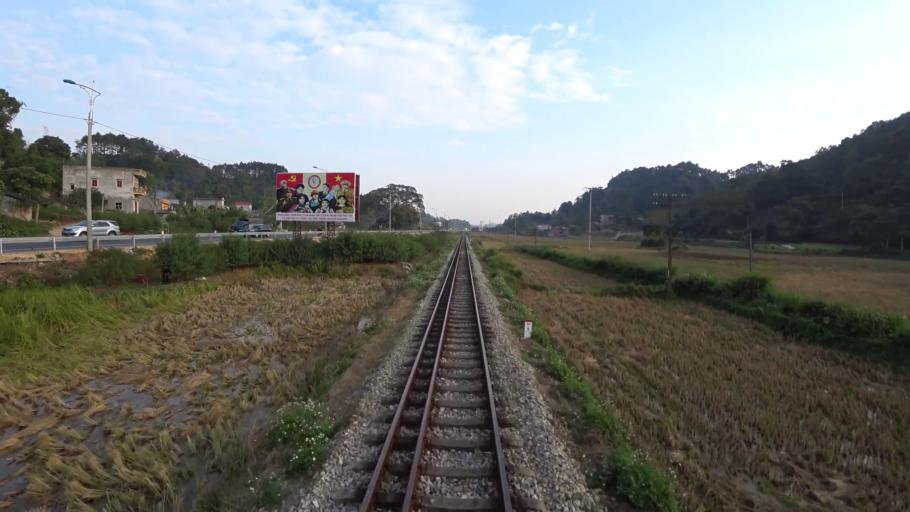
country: VN
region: Lang Son
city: Thi Tran Cao Loc
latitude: 21.9032
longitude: 106.7373
